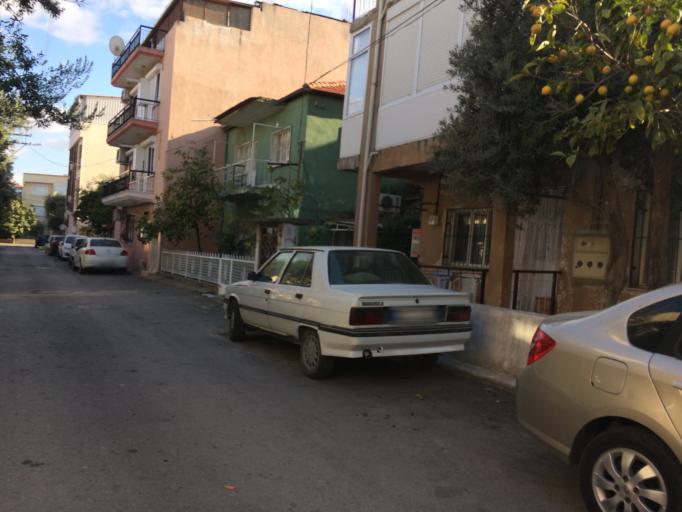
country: TR
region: Izmir
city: Karsiyaka
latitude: 38.4909
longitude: 27.0600
